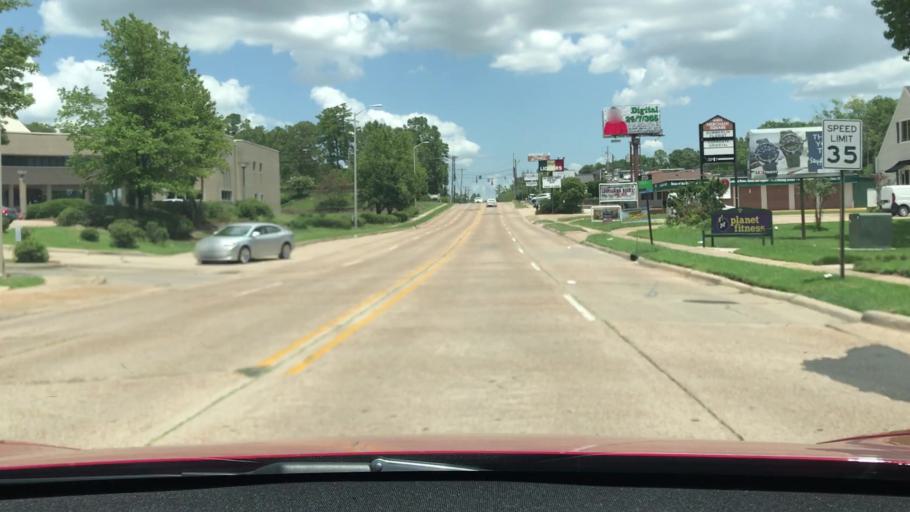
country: US
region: Louisiana
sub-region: Bossier Parish
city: Bossier City
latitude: 32.4475
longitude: -93.7460
